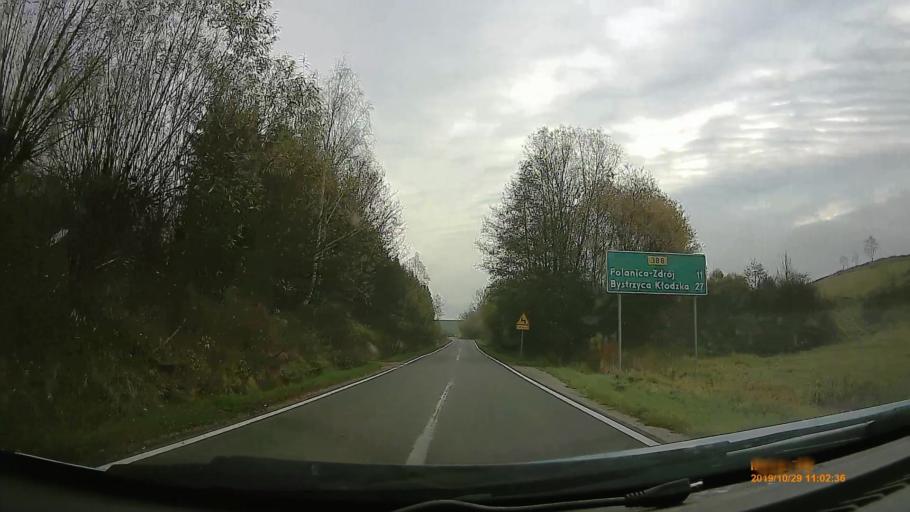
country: PL
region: Lower Silesian Voivodeship
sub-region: Powiat klodzki
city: Radkow
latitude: 50.4881
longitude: 16.4614
